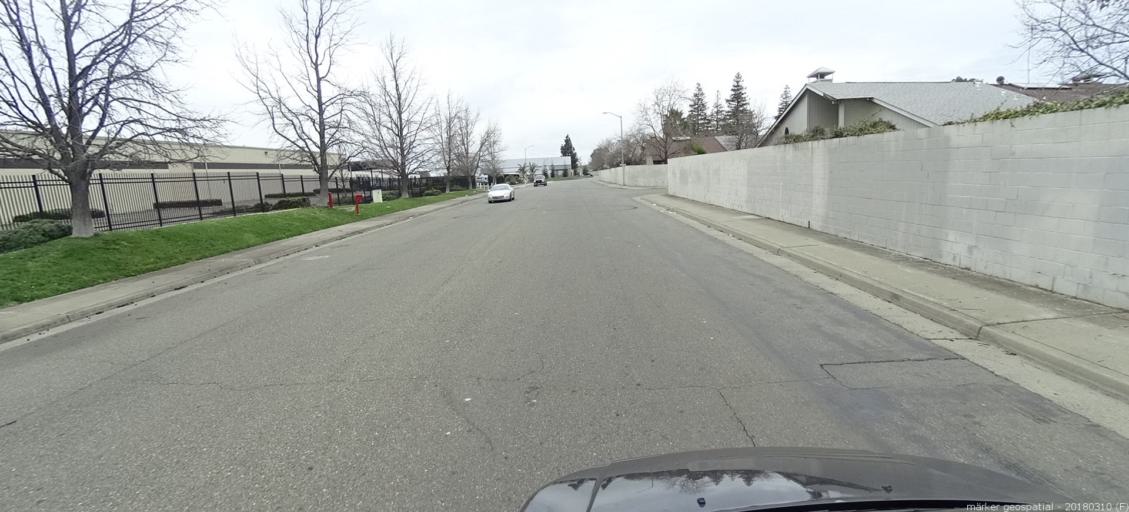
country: US
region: California
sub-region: Sacramento County
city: Florin
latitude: 38.4771
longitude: -121.3882
